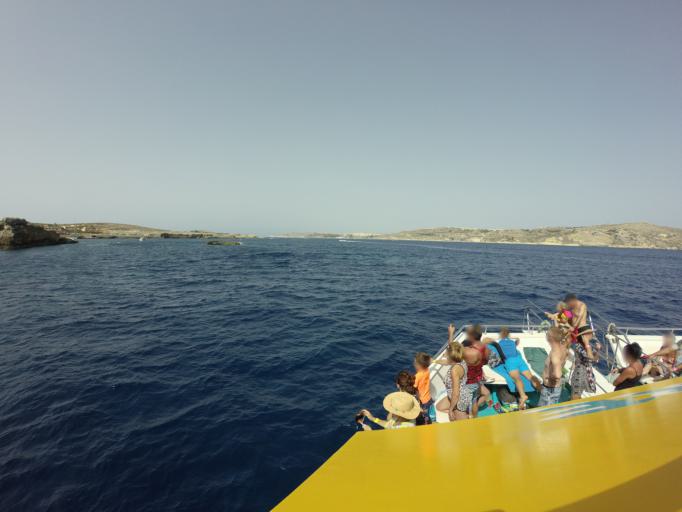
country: MT
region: Il-Qala
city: Qala
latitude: 36.0211
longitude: 14.3390
